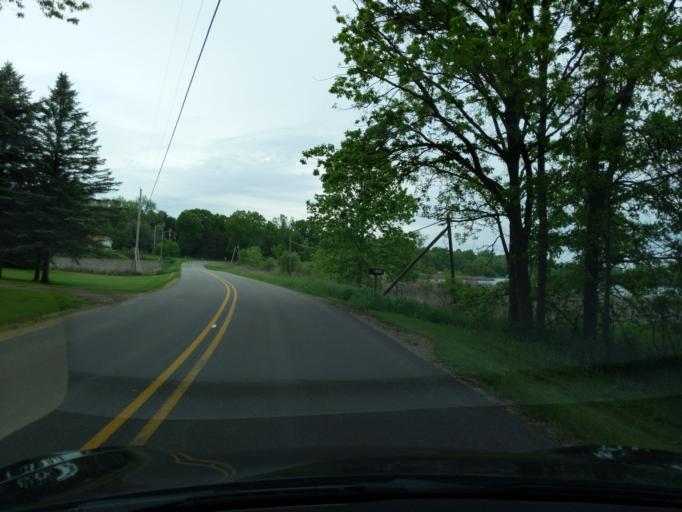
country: US
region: Michigan
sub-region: Jackson County
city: Jackson
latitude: 42.3546
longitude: -84.3488
